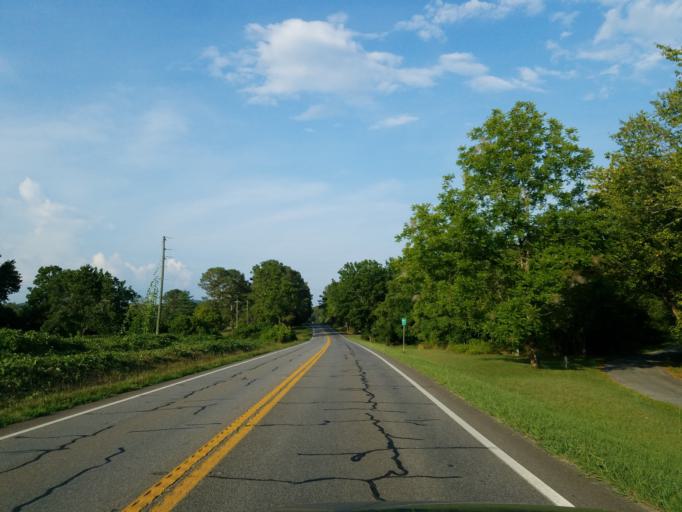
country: US
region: Georgia
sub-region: Pickens County
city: Jasper
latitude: 34.5170
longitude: -84.5378
